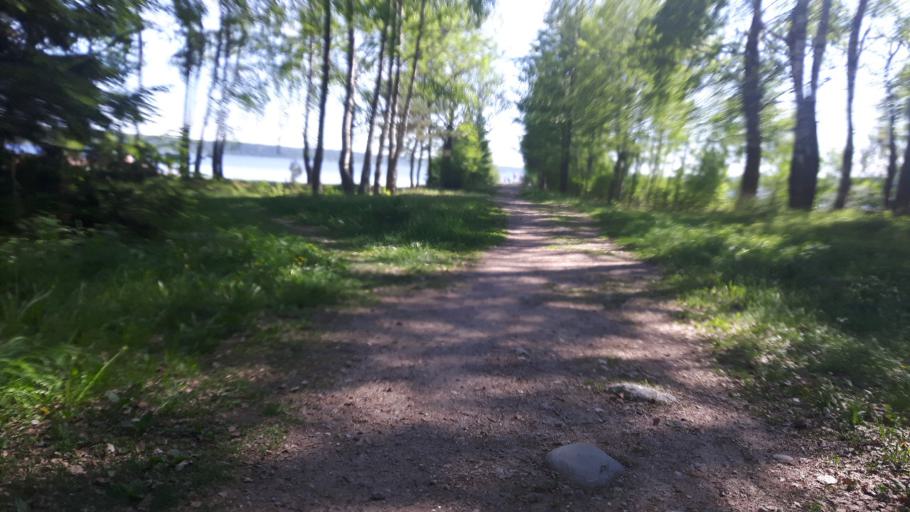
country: RU
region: Leningrad
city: Sista-Palkino
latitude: 59.7619
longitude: 28.7400
